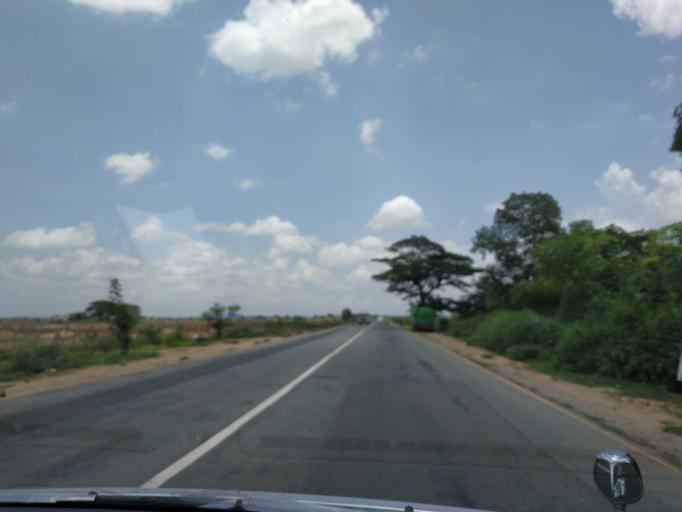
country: MM
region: Bago
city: Thanatpin
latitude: 17.4603
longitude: 96.5983
